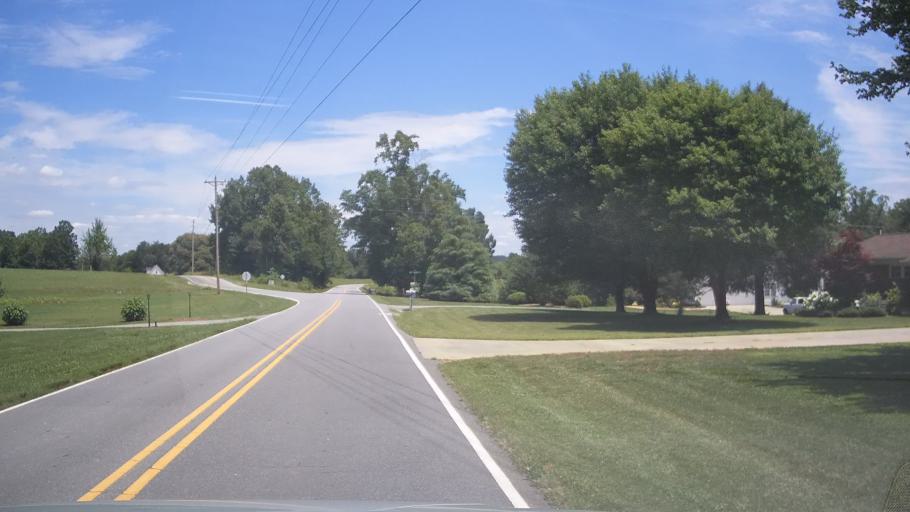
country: US
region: North Carolina
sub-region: Burke County
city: Glen Alpine
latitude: 35.6428
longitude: -81.7922
